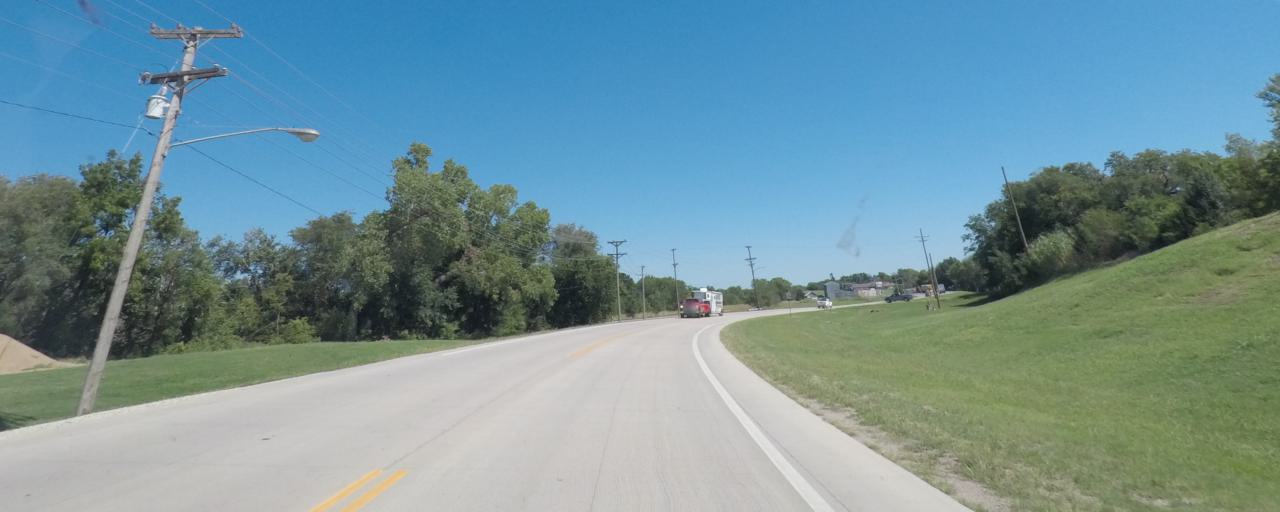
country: US
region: Kansas
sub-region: Sumner County
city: Wellington
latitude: 37.2624
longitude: -97.4070
